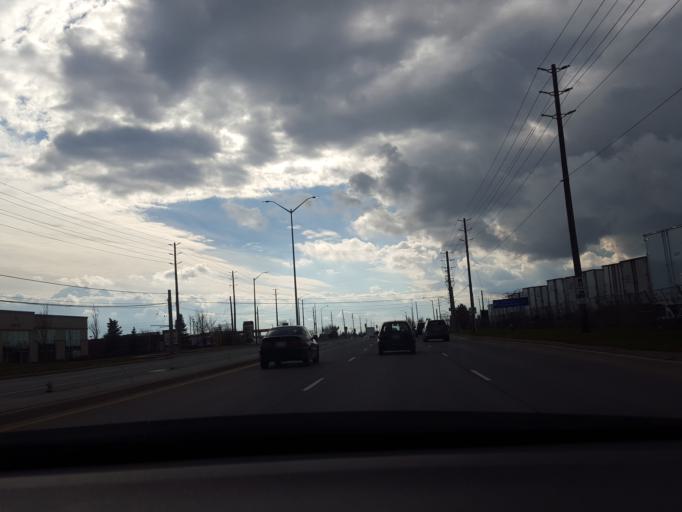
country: CA
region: Ontario
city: Brampton
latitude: 43.6482
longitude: -79.7039
